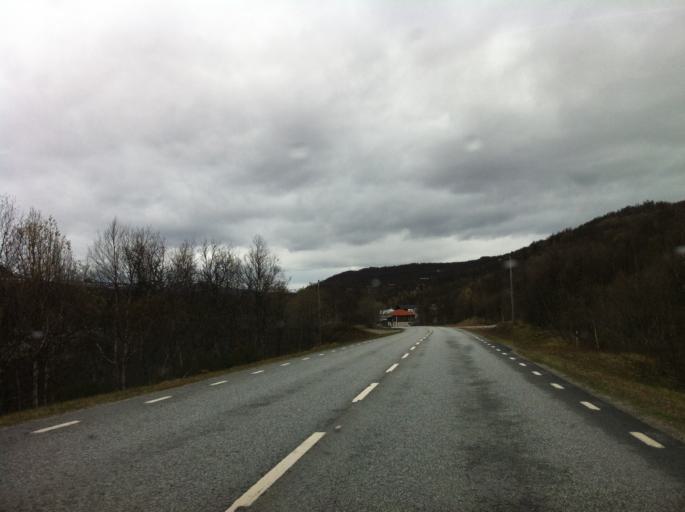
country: NO
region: Sor-Trondelag
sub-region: Tydal
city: Aas
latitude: 62.5707
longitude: 12.2344
